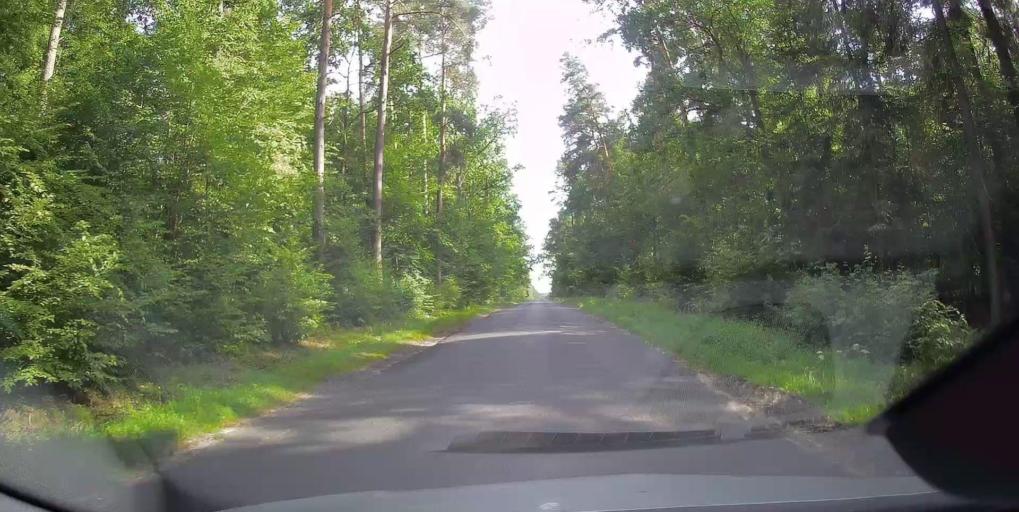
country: PL
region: Lodz Voivodeship
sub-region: Powiat opoczynski
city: Mniszkow
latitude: 51.4349
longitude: 20.0239
